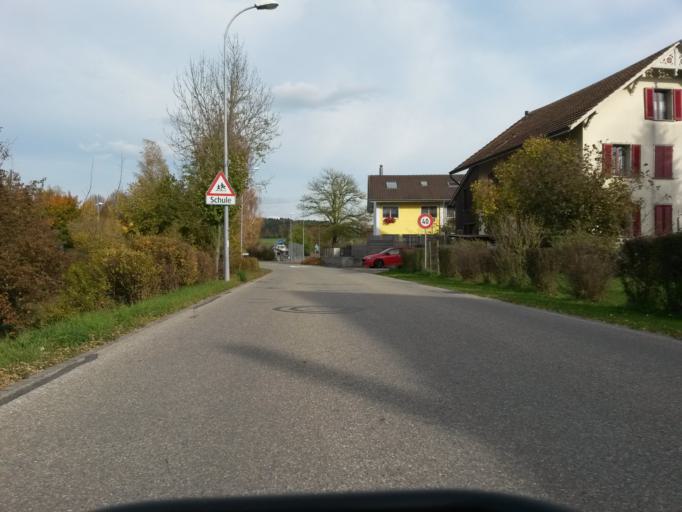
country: CH
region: Bern
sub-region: Emmental District
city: Koppigen
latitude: 47.1335
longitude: 7.6050
